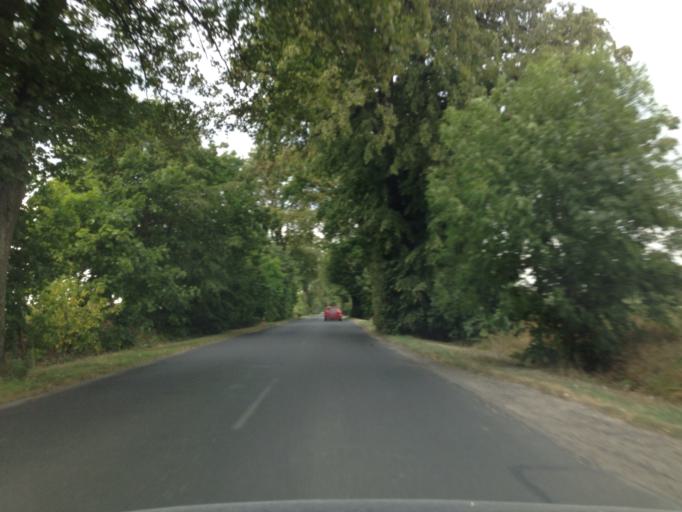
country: PL
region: Kujawsko-Pomorskie
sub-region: Powiat torunski
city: Chelmza
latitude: 53.3074
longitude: 18.5537
